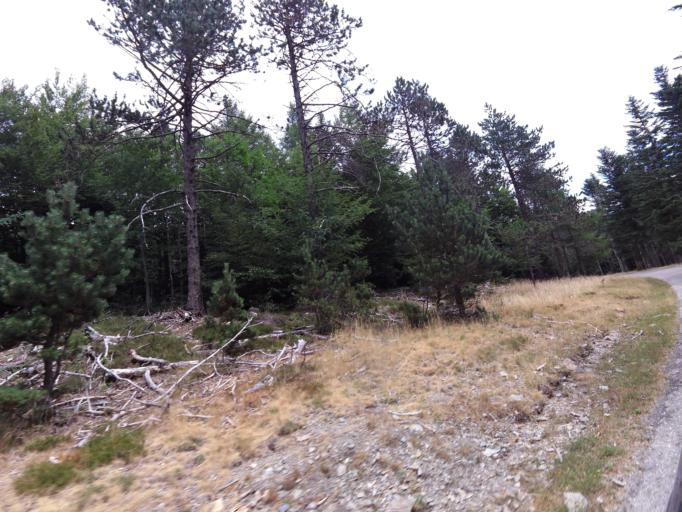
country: FR
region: Languedoc-Roussillon
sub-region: Departement du Gard
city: Valleraugue
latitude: 44.0653
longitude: 3.5972
